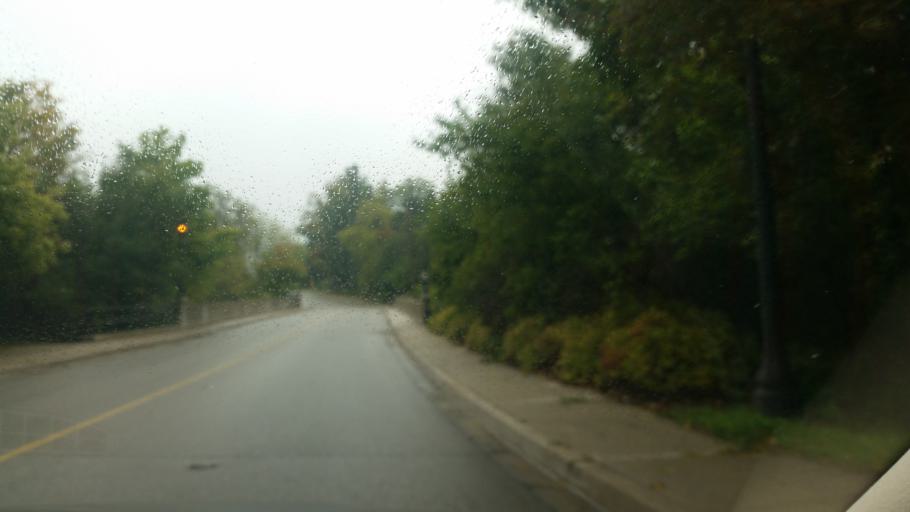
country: CA
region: Ontario
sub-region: Wellington County
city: Guelph
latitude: 43.6847
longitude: -80.4343
